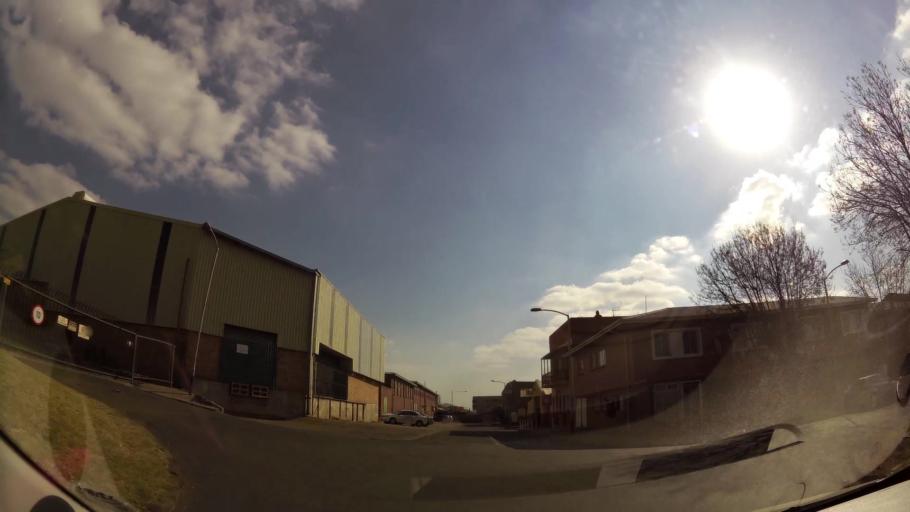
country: ZA
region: Gauteng
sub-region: West Rand District Municipality
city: Krugersdorp
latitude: -26.1079
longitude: 27.7739
